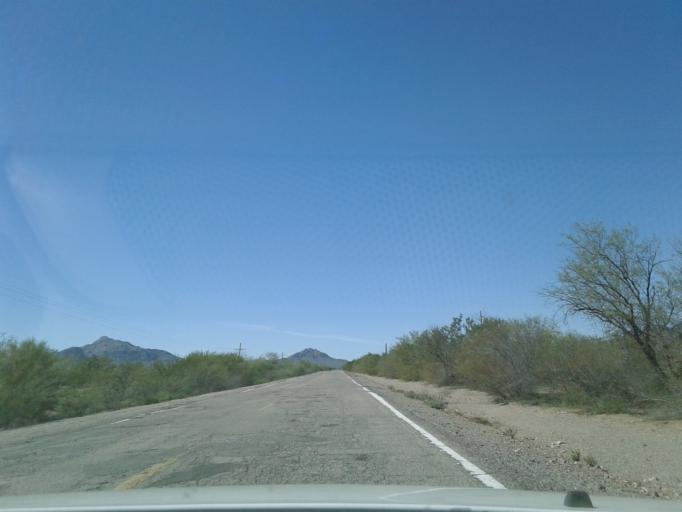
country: US
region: Arizona
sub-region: Pima County
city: Avra Valley
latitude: 32.3711
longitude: -111.4023
